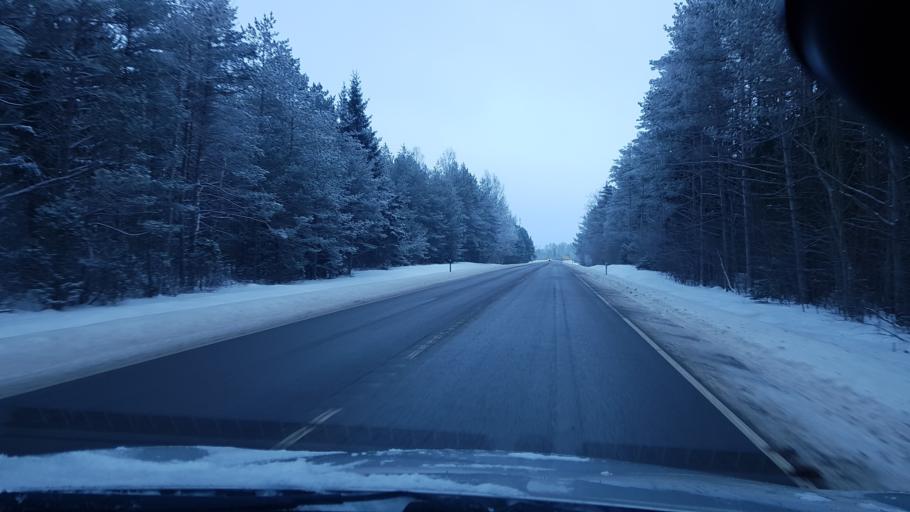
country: EE
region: Harju
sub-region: Keila linn
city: Keila
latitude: 59.3304
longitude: 24.2964
